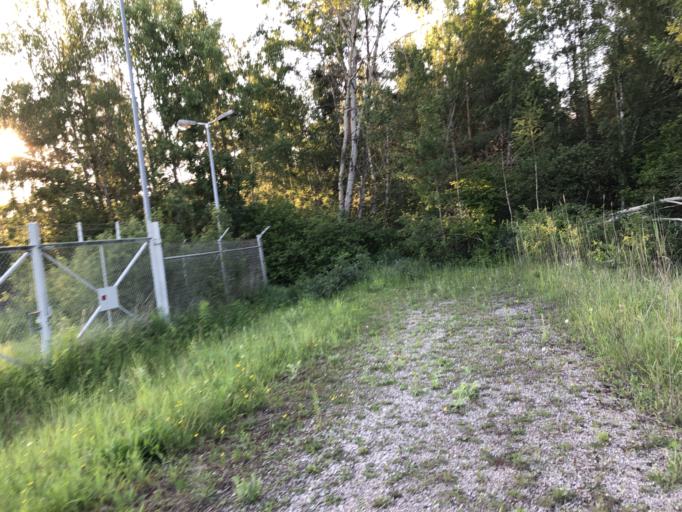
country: DE
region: Bavaria
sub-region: Upper Franconia
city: Memmelsdorf
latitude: 49.9163
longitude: 10.9471
